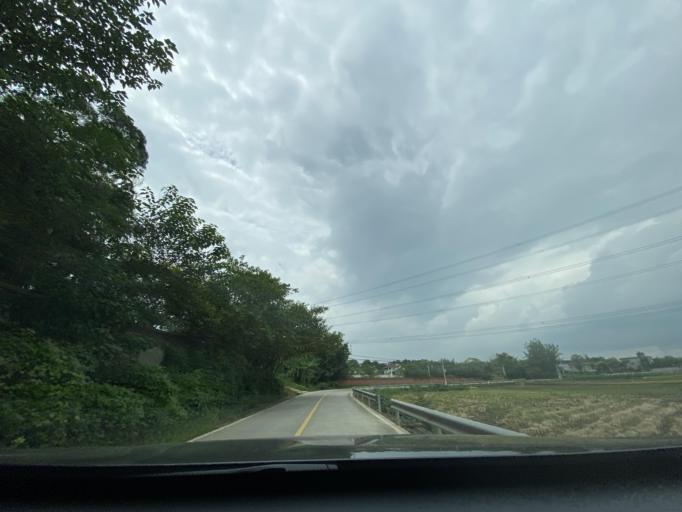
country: CN
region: Sichuan
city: Wujin
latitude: 30.3742
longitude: 103.9691
